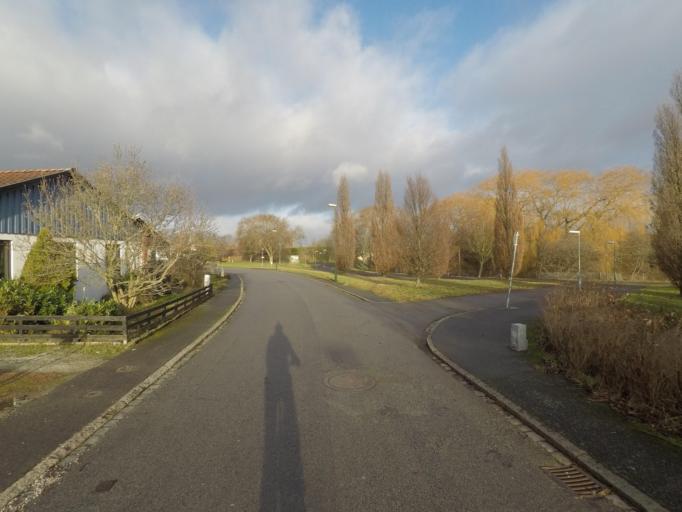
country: SE
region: Skane
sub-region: Burlovs Kommun
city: Arloev
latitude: 55.5932
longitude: 13.0811
